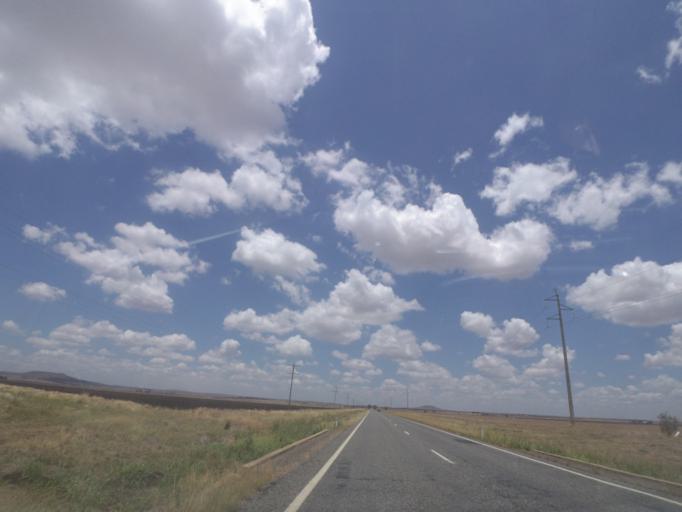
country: AU
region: Queensland
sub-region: Toowoomba
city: Top Camp
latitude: -27.9043
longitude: 151.9774
